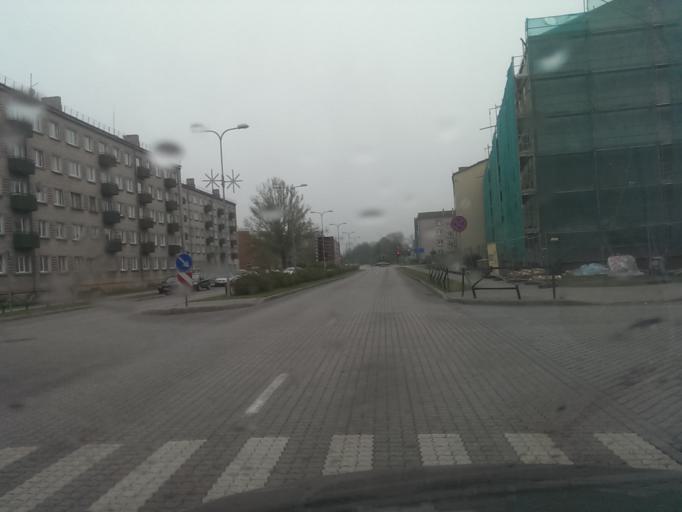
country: LV
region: Ventspils
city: Ventspils
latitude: 57.3911
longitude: 21.5736
